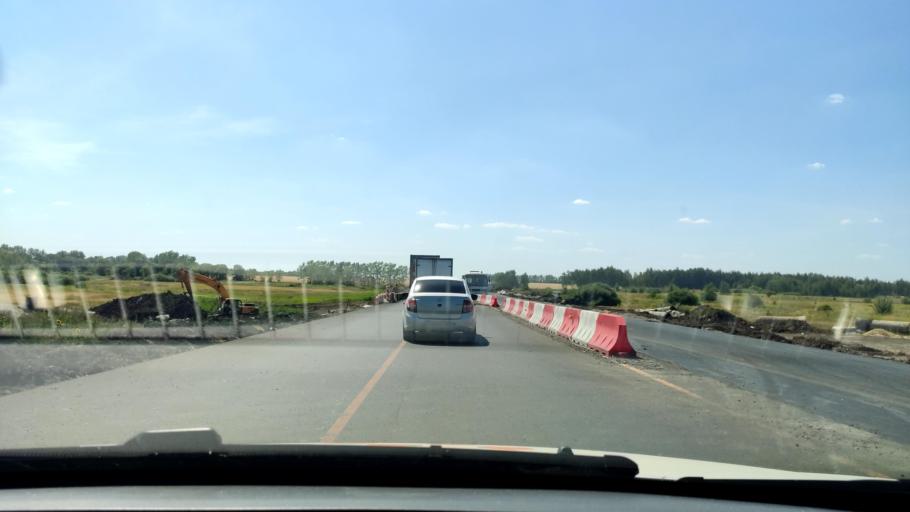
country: RU
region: Voronezj
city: Pereleshino
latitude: 51.7137
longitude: 40.0079
